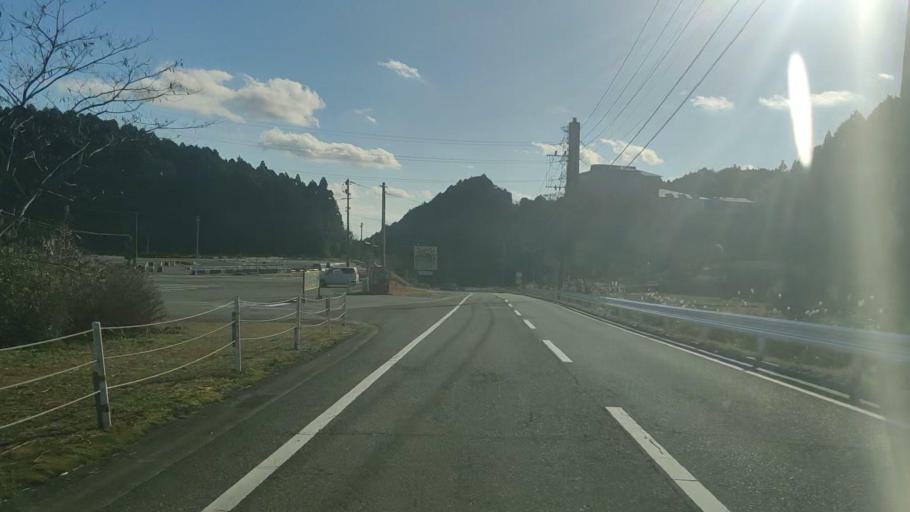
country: JP
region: Saga Prefecture
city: Kanzakimachi-kanzaki
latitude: 33.4007
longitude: 130.2721
